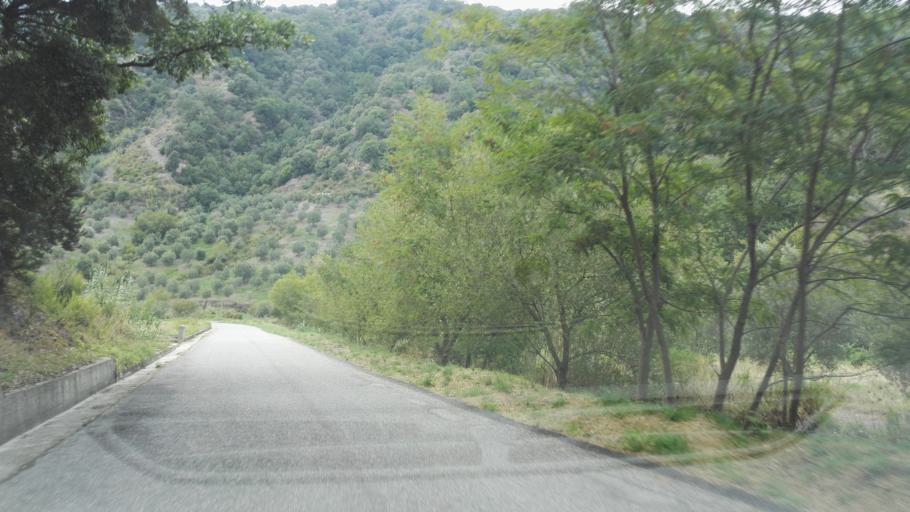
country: IT
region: Calabria
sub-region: Provincia di Reggio Calabria
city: Caulonia
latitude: 38.4348
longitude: 16.4008
